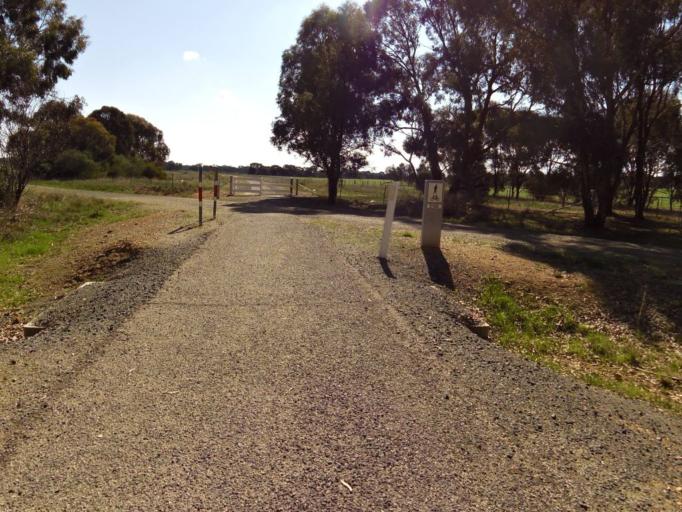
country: AU
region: New South Wales
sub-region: Corowa Shire
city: Corowa
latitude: -36.0368
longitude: 146.4512
